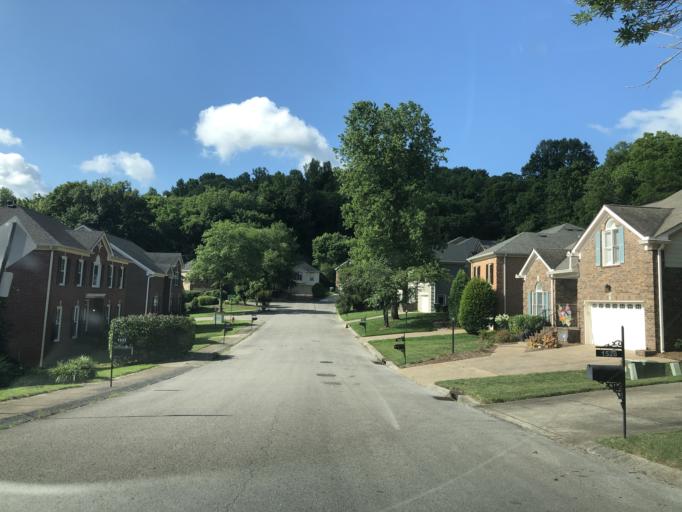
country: US
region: Tennessee
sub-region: Cheatham County
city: Pegram
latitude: 36.0619
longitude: -86.9570
